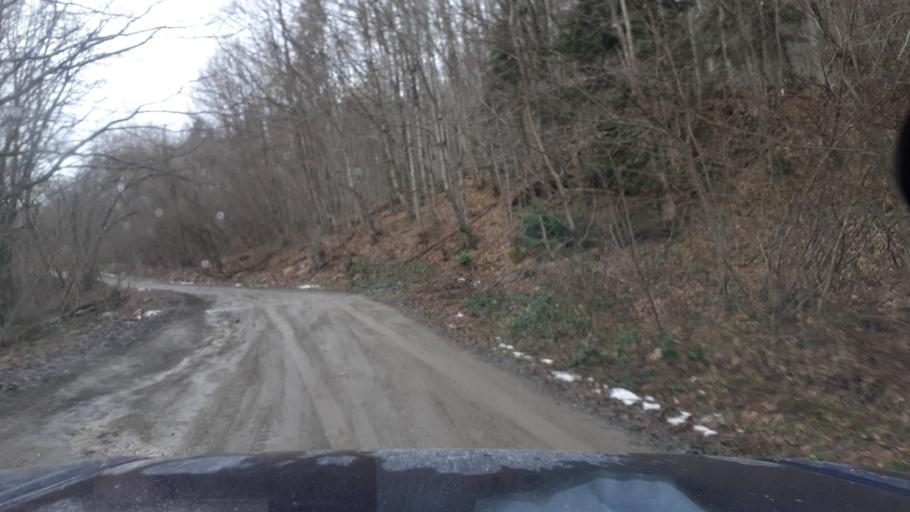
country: RU
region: Krasnodarskiy
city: Neftegorsk
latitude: 44.0687
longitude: 39.7295
